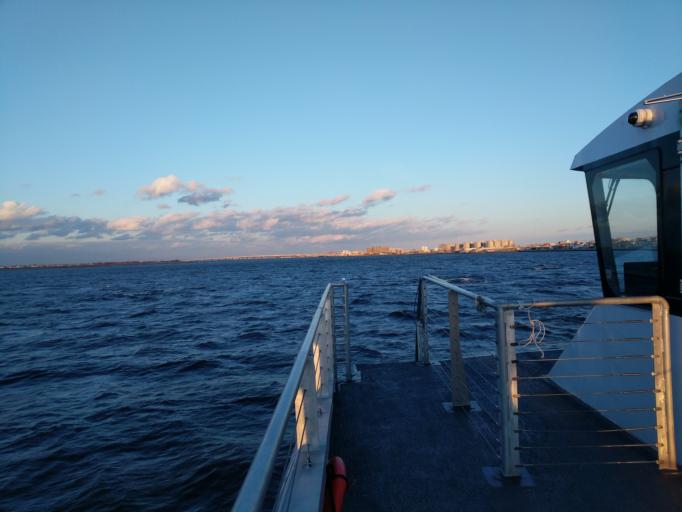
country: US
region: New York
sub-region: Kings County
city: East New York
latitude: 40.5836
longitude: -73.8520
